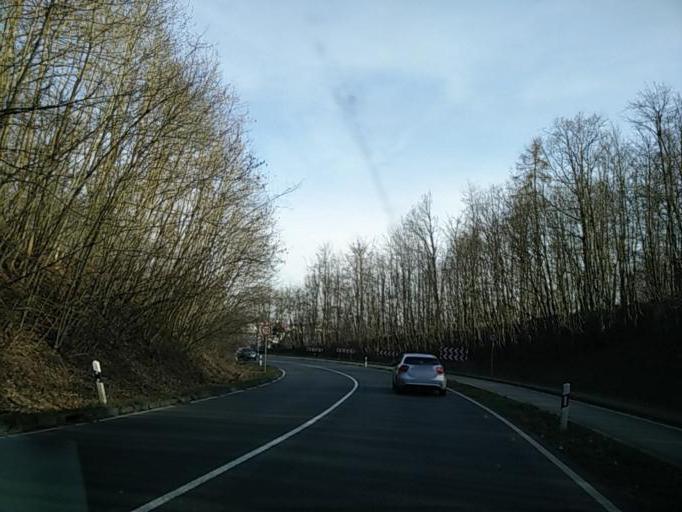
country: DE
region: Baden-Wuerttemberg
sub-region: Regierungsbezirk Stuttgart
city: Holzgerlingen
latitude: 48.6604
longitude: 9.0089
